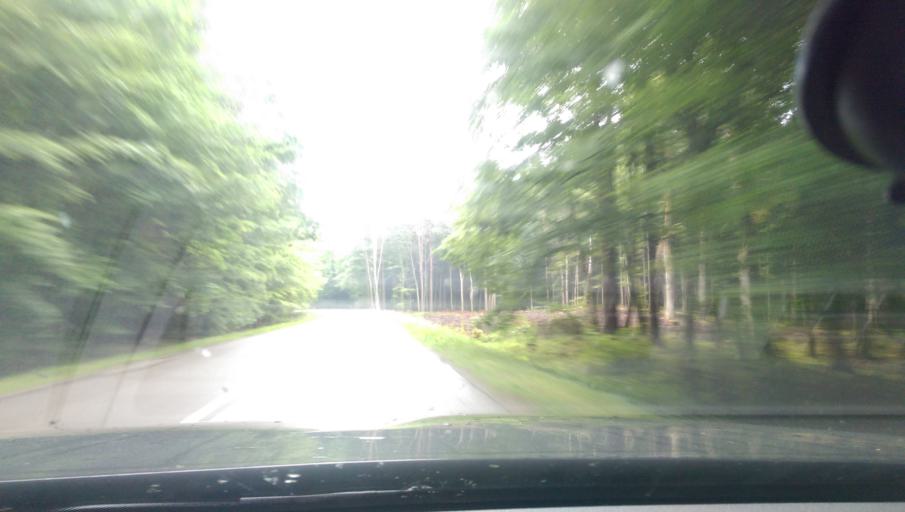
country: PL
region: Warmian-Masurian Voivodeship
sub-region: Powiat piski
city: Ruciane-Nida
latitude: 53.7029
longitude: 21.4504
